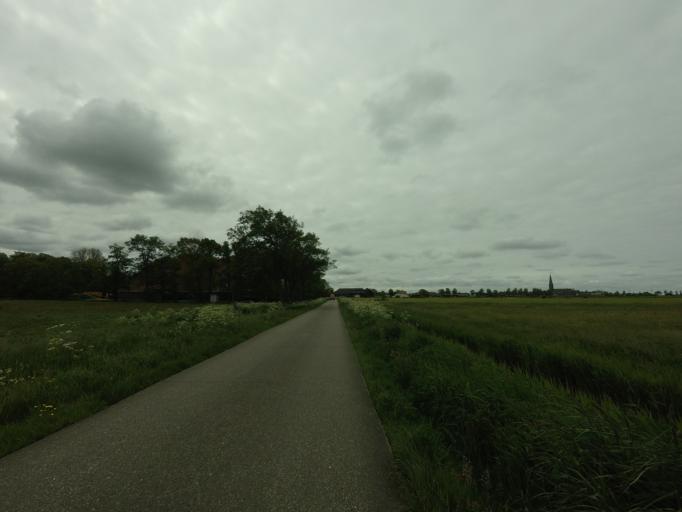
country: NL
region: Friesland
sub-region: Sudwest Fryslan
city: Workum
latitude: 52.9886
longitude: 5.4572
